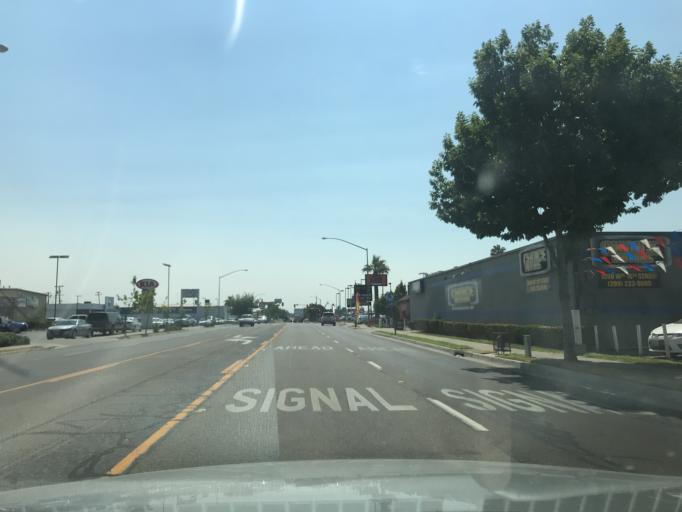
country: US
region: California
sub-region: Merced County
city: Merced
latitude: 37.3068
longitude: -120.5014
